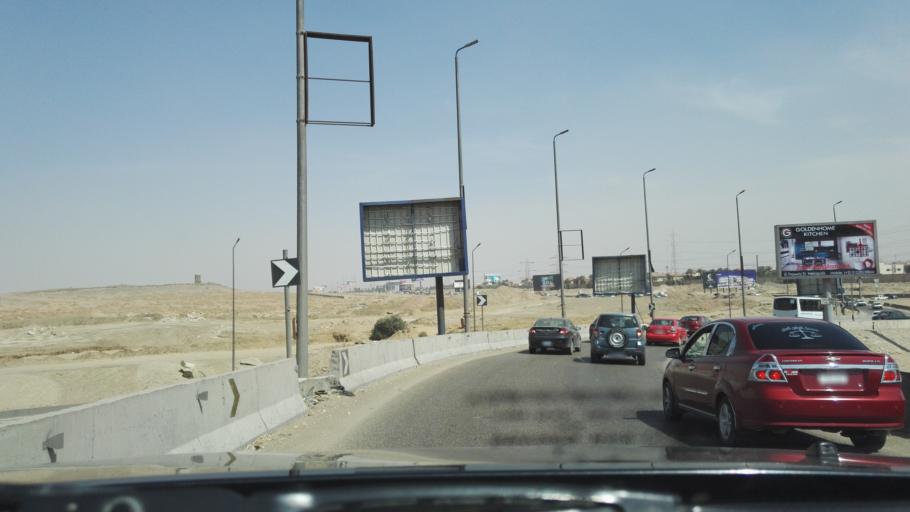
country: EG
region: Muhafazat al Qalyubiyah
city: Al Khankah
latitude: 30.0817
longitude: 31.4371
